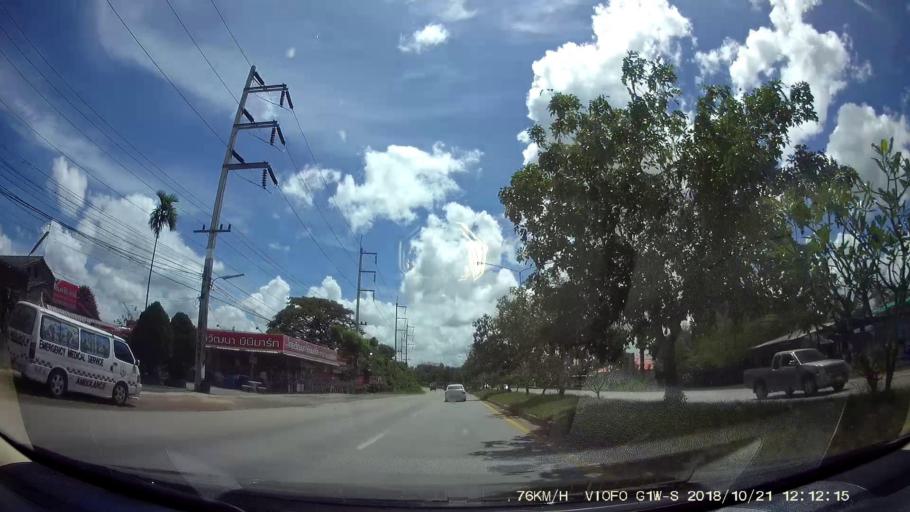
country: TH
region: Chaiyaphum
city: Chatturat
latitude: 15.4090
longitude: 101.8344
